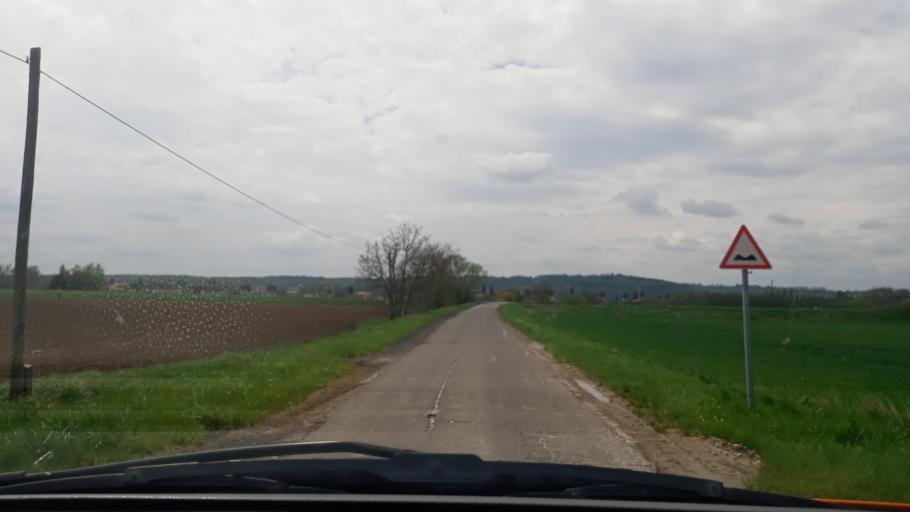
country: HU
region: Baranya
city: Sasd
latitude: 46.2602
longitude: 18.1176
